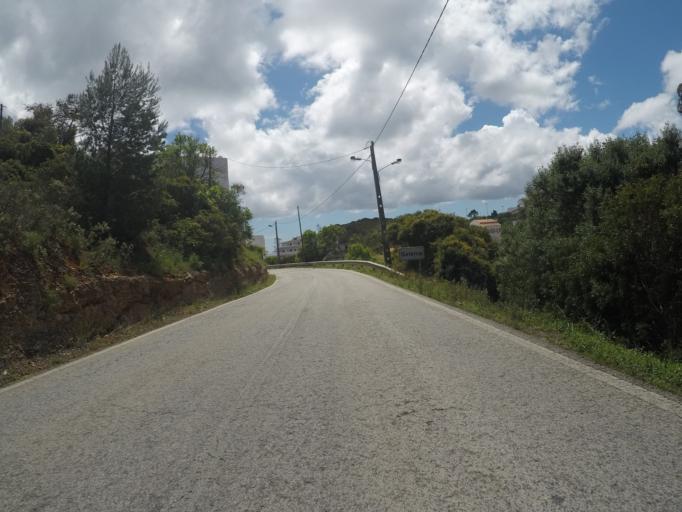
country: PT
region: Faro
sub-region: Vila do Bispo
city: Vila do Bispo
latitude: 37.0672
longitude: -8.8250
